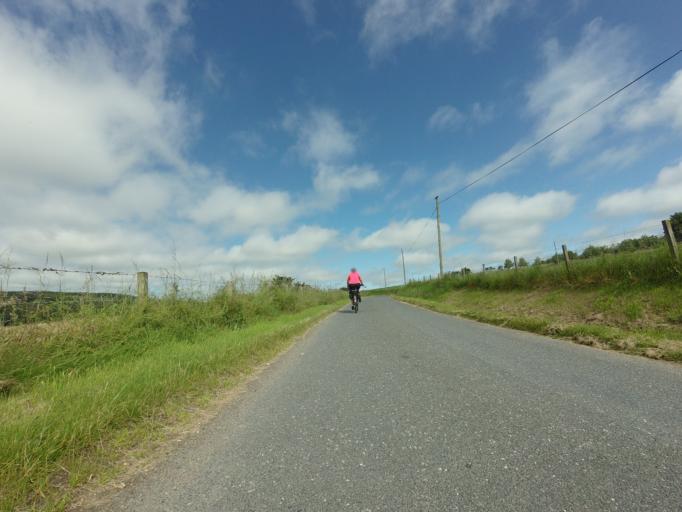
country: GB
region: Scotland
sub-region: Aberdeenshire
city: Turriff
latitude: 57.5675
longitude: -2.4960
